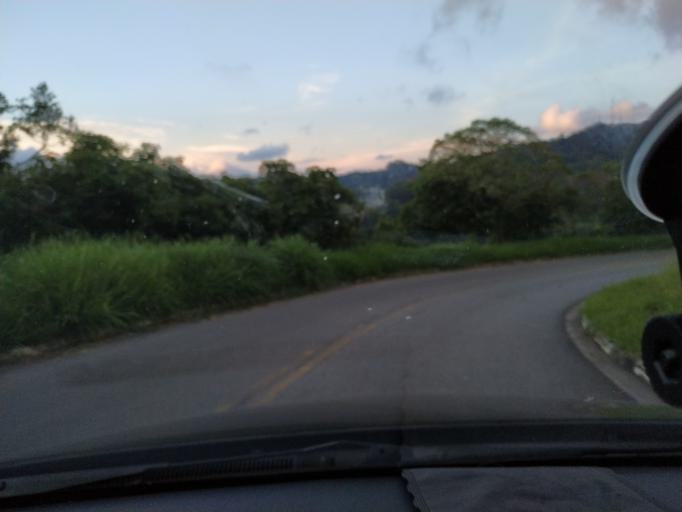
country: BR
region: Sao Paulo
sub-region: Campos Do Jordao
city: Campos do Jordao
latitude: -22.8081
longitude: -45.6340
